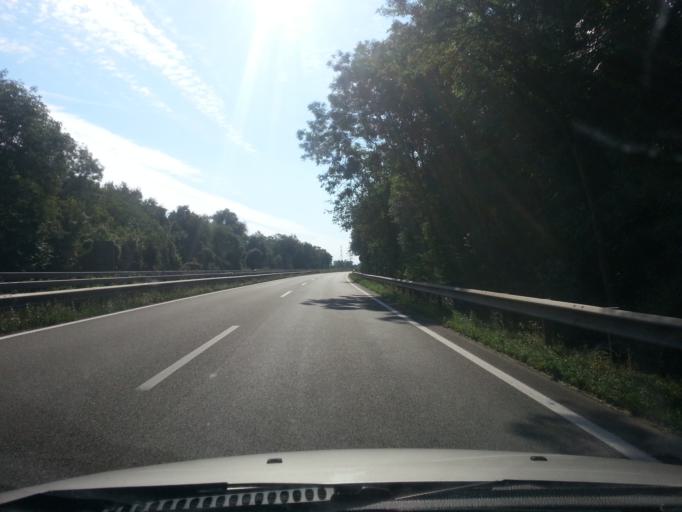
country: DE
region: Rheinland-Pfalz
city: Bobenheim-Roxheim
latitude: 49.6048
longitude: 8.3884
